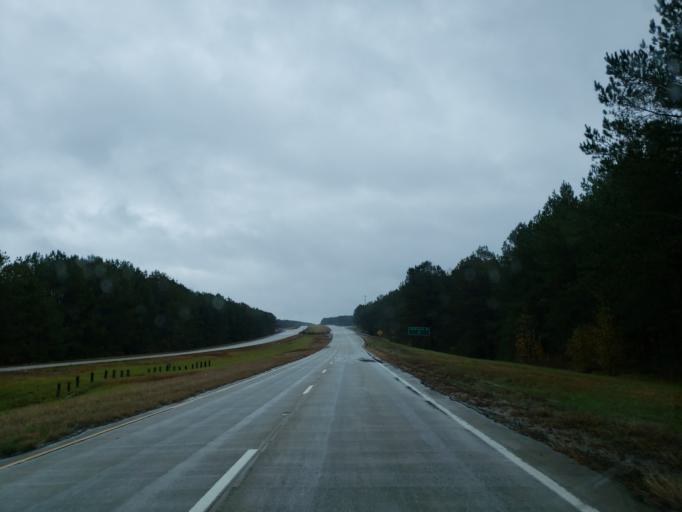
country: US
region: Mississippi
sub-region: Lauderdale County
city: Meridian
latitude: 32.3279
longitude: -88.6697
